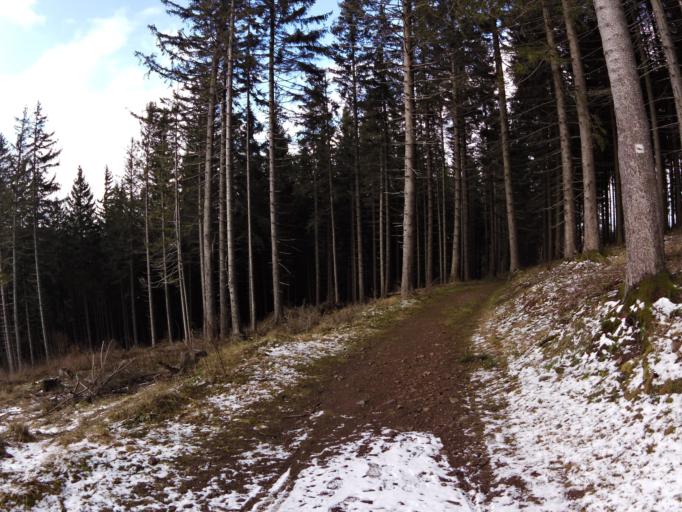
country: DE
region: Thuringia
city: Ilmenau
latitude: 50.6665
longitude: 10.9049
